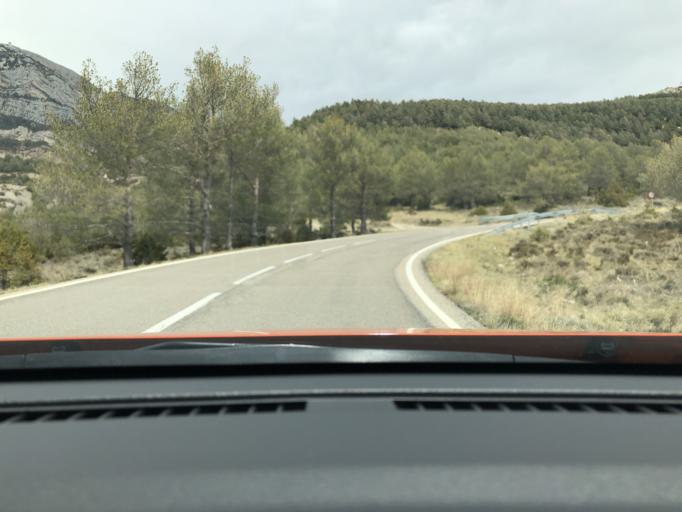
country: ES
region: Catalonia
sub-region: Provincia de Lleida
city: Olius
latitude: 42.1292
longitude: 1.5441
